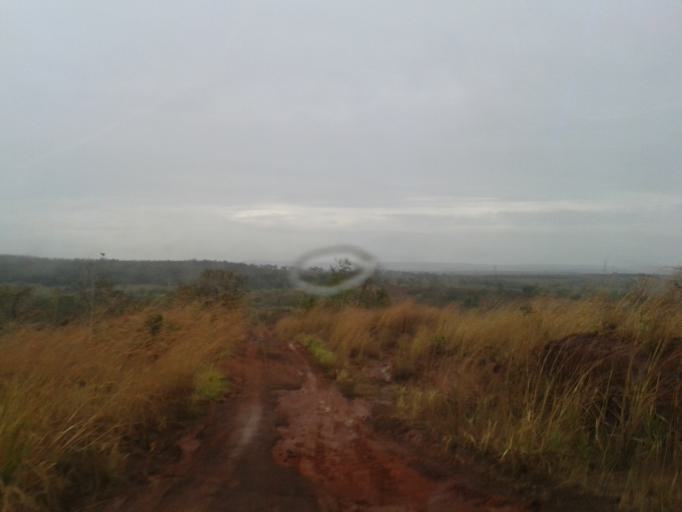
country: BR
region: Minas Gerais
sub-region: Campina Verde
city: Campina Verde
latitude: -19.3232
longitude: -49.5133
